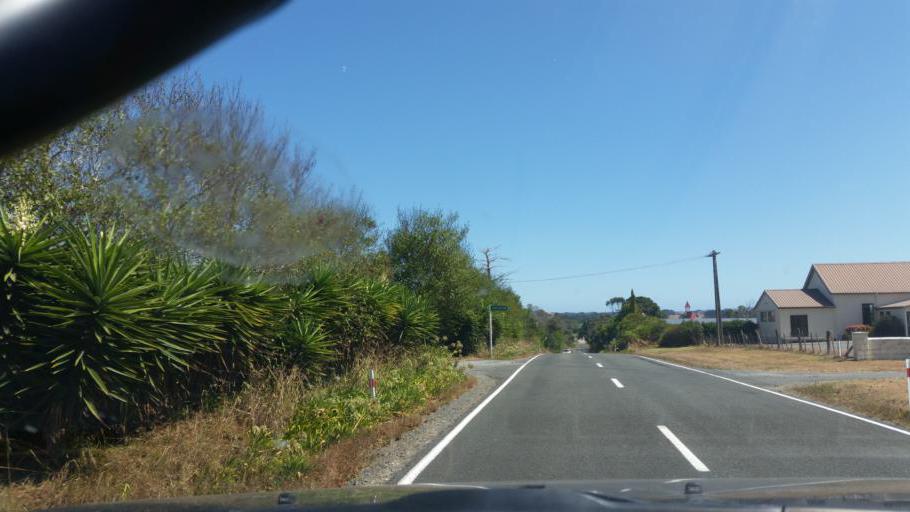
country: NZ
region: Northland
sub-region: Kaipara District
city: Dargaville
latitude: -36.0114
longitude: 173.9385
